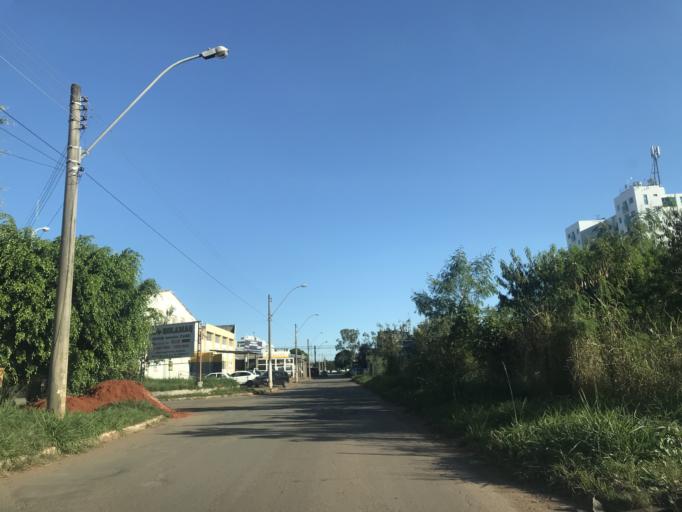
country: BR
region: Federal District
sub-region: Brasilia
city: Brasilia
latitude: -15.8242
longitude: -47.9584
